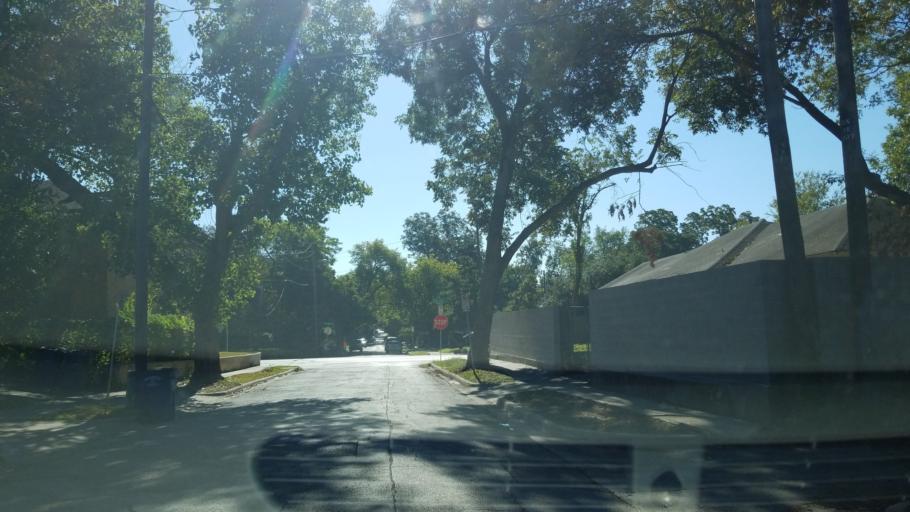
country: US
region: Texas
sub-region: Dallas County
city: Highland Park
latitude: 32.8107
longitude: -96.7641
